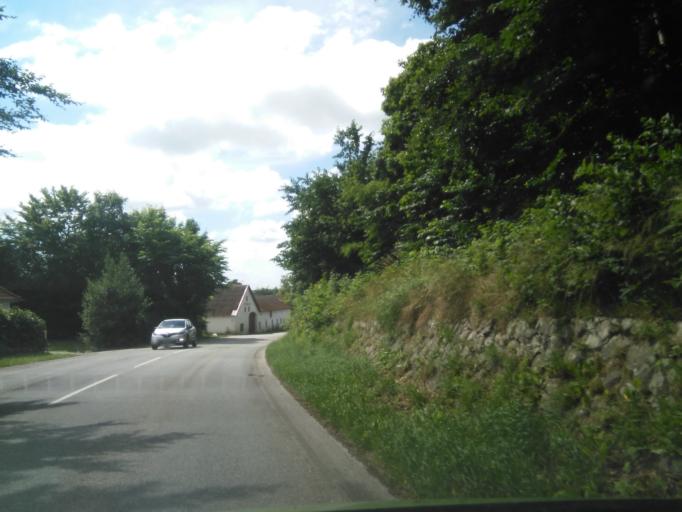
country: DK
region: Central Jutland
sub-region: Syddjurs Kommune
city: Ronde
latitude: 56.2170
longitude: 10.4866
